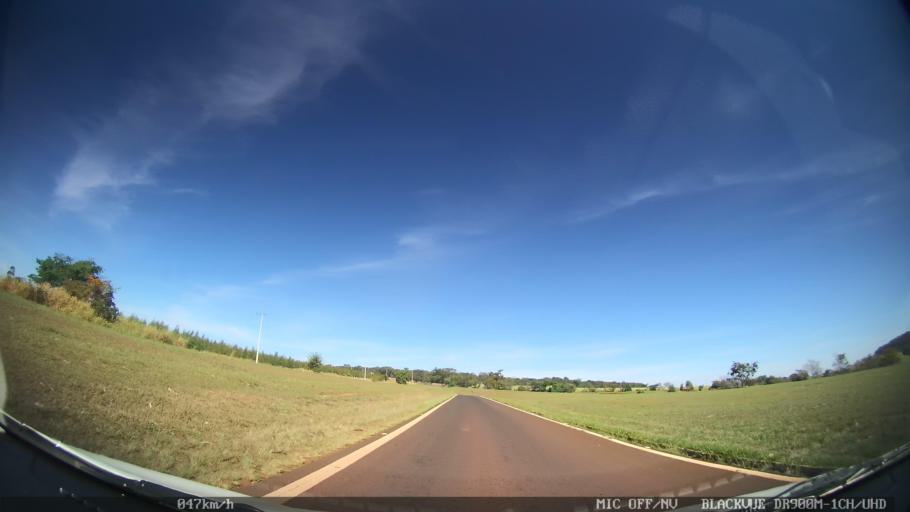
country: BR
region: Sao Paulo
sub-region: Sao Simao
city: Sao Simao
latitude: -21.5280
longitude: -47.6408
